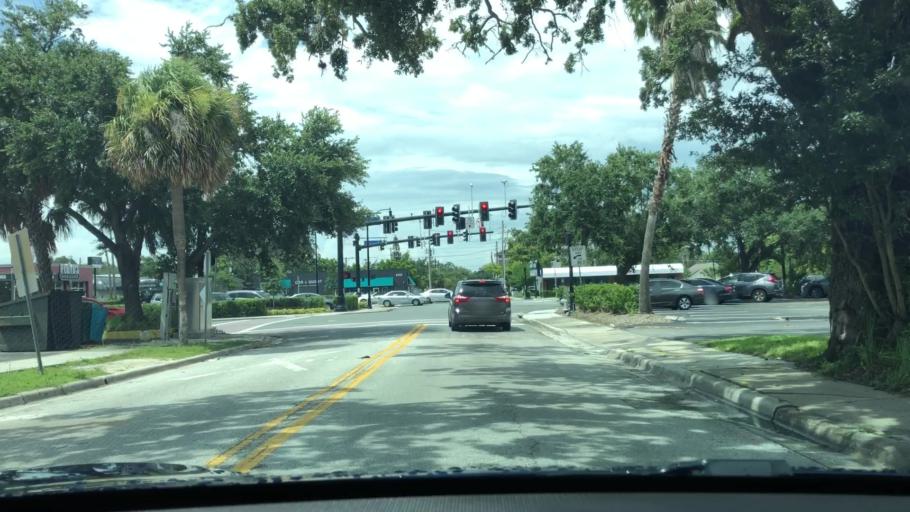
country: US
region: Florida
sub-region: Orange County
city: Winter Park
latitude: 28.5923
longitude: -81.3568
